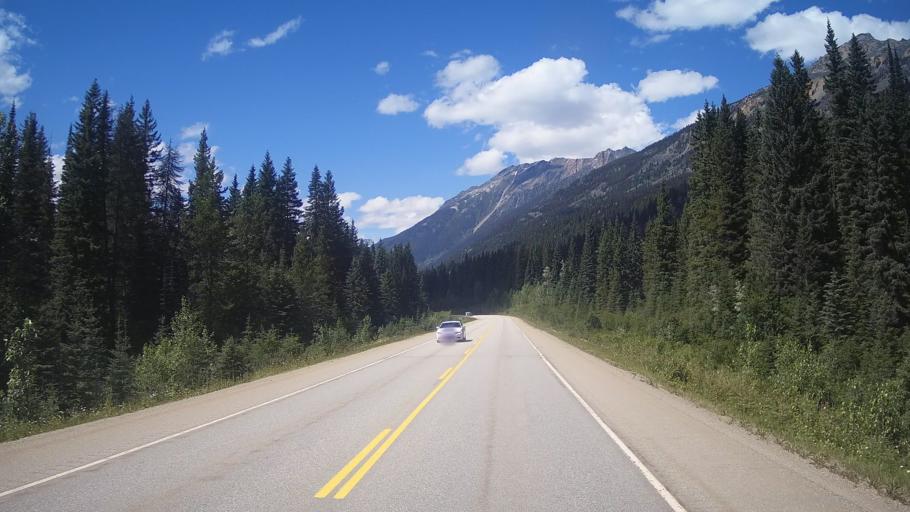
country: CA
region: Alberta
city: Grande Cache
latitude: 52.9984
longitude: -119.0270
